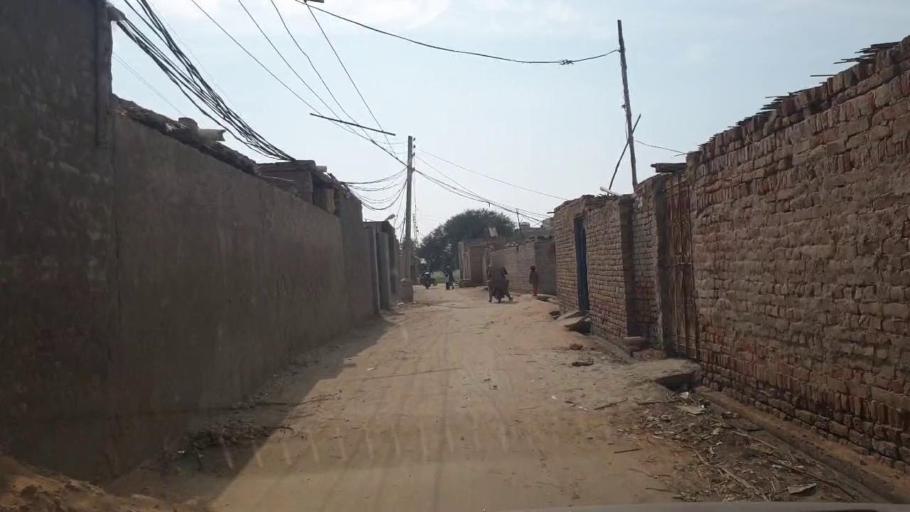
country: PK
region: Sindh
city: Shahdadpur
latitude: 25.8962
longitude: 68.6440
